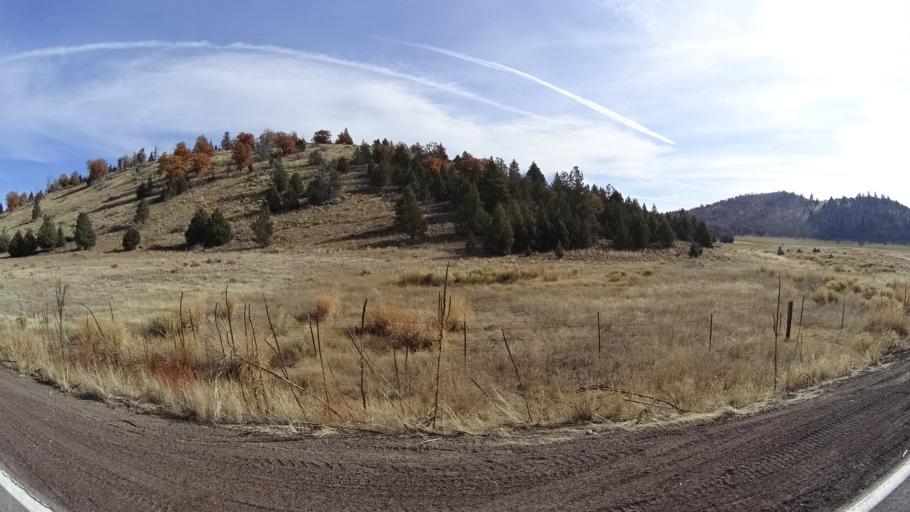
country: US
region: California
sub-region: Siskiyou County
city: Weed
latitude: 41.4885
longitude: -122.4058
